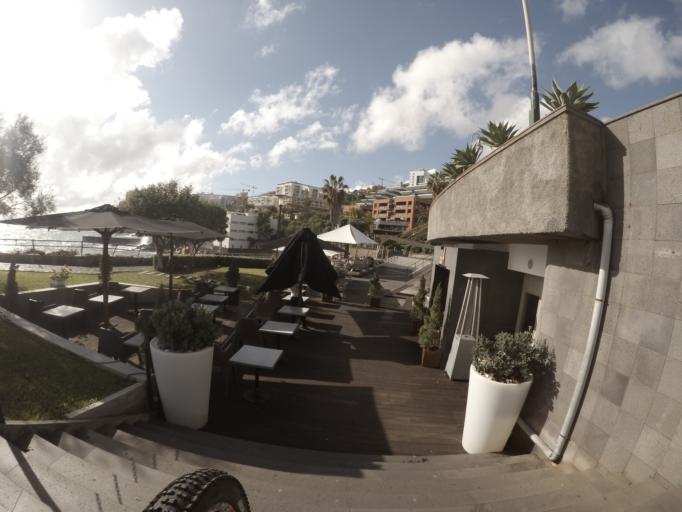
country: PT
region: Madeira
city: Camara de Lobos
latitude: 32.6365
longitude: -16.9341
